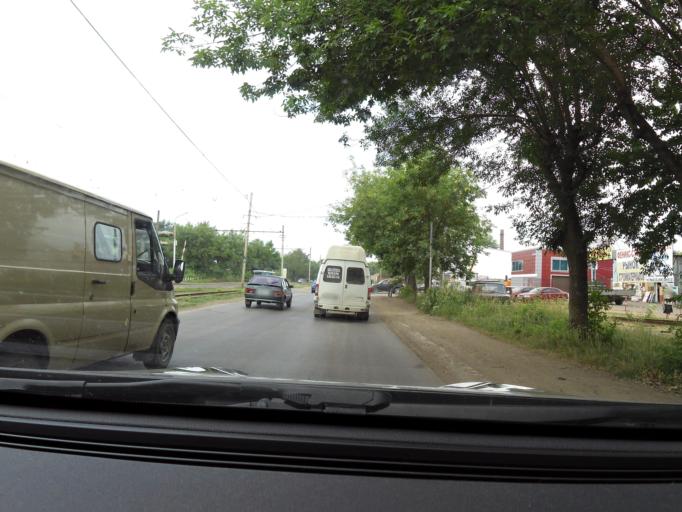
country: RU
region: Bashkortostan
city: Ufa
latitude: 54.7991
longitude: 56.0925
